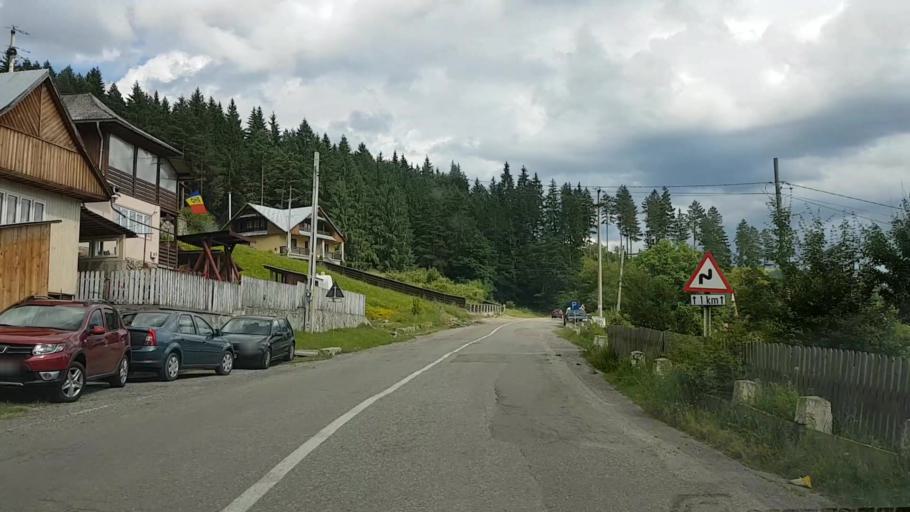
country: RO
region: Neamt
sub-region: Comuna Hangu
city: Hangu
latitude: 47.0097
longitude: 26.0881
